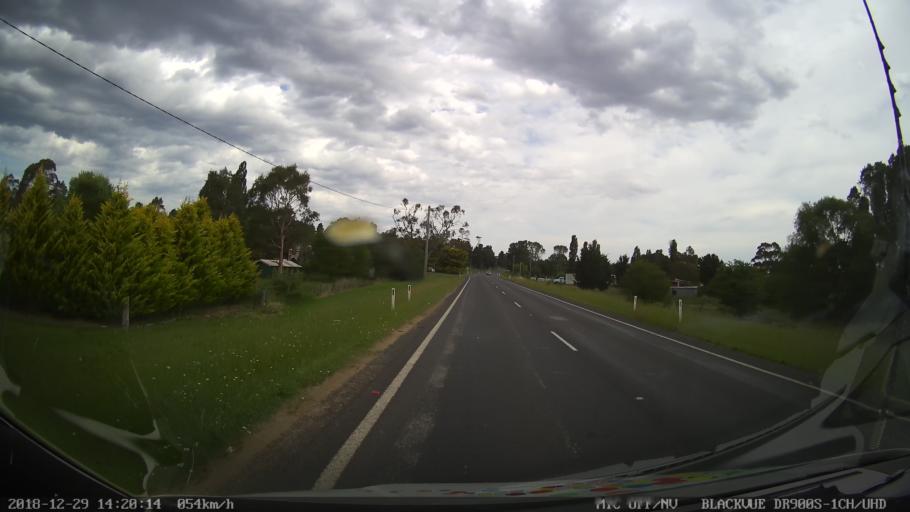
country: AU
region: New South Wales
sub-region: Cooma-Monaro
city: Cooma
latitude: -36.5064
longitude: 149.2853
